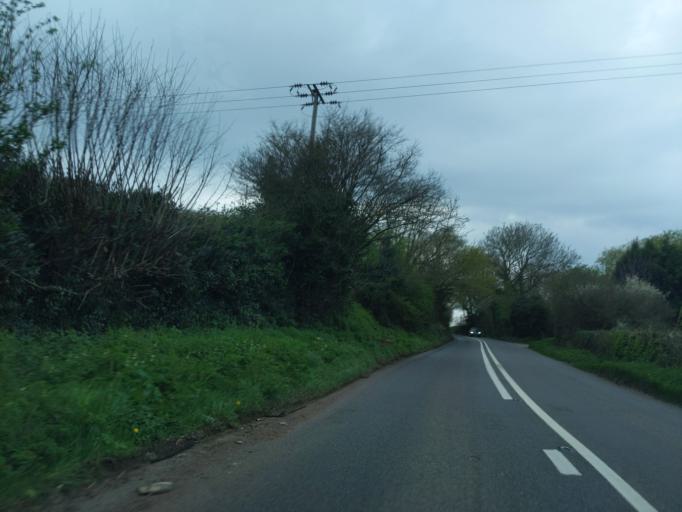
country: GB
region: England
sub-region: Devon
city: Crediton
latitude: 50.7974
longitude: -3.6886
